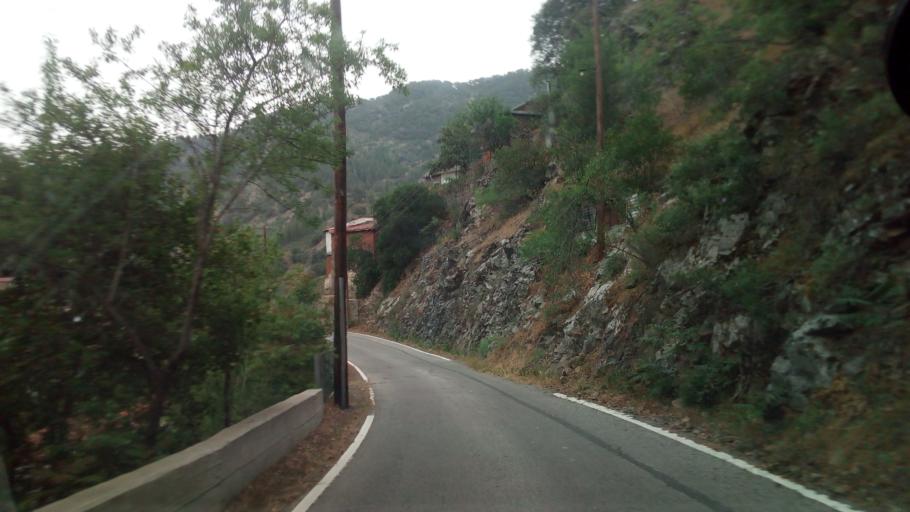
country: CY
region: Lefkosia
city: Kakopetria
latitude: 34.9605
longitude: 32.7514
